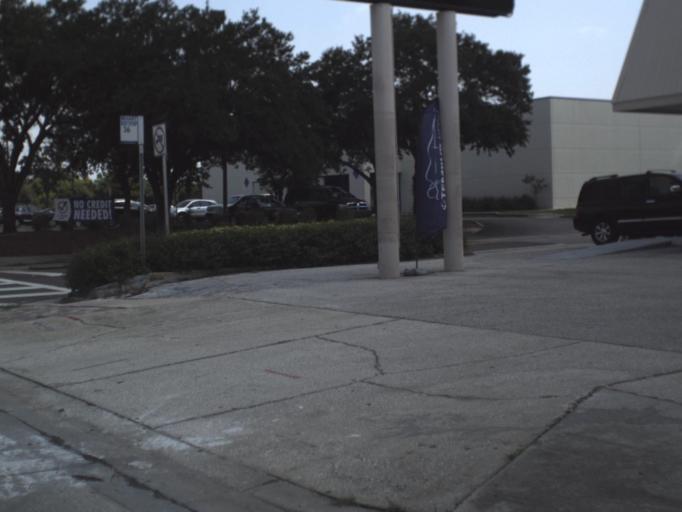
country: US
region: Florida
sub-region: Hillsborough County
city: Tampa
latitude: 27.9500
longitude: -82.5055
